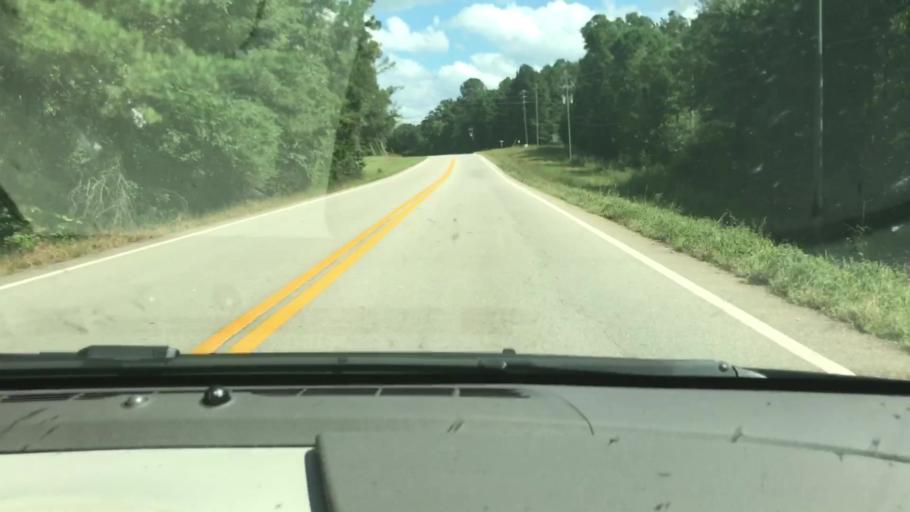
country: US
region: Georgia
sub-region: Troup County
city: La Grange
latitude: 32.9148
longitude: -85.0207
